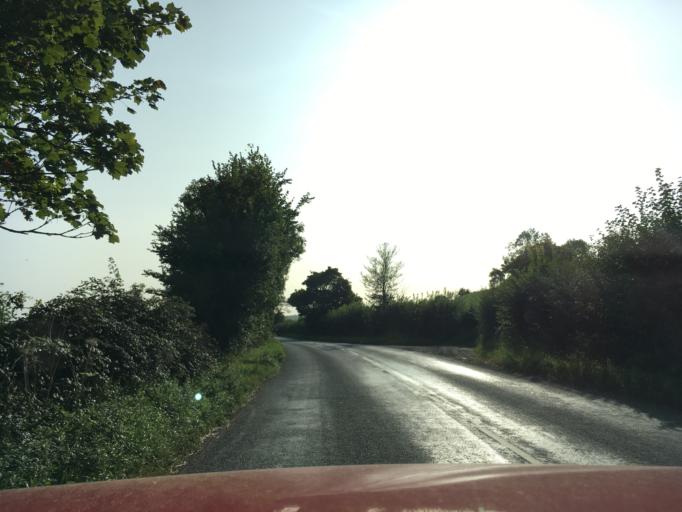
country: GB
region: England
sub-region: Gloucestershire
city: Tewkesbury
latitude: 51.9487
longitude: -2.1964
